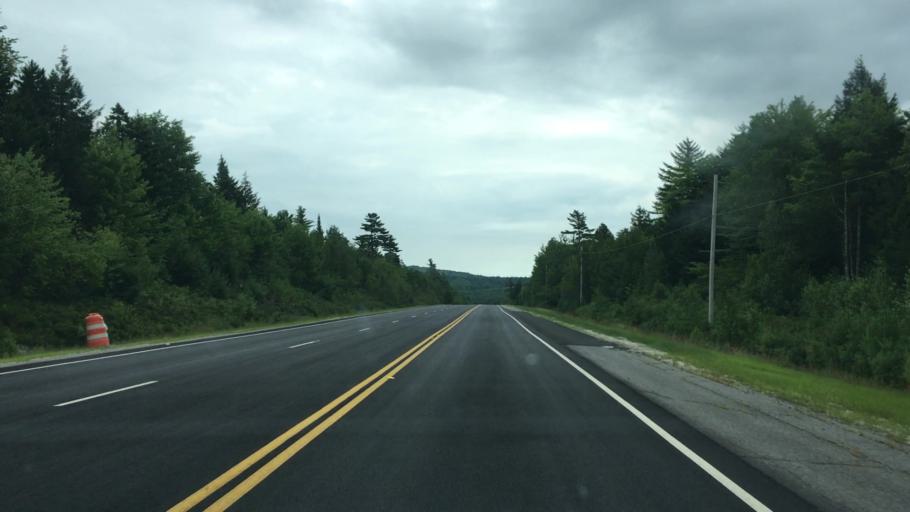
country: US
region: Maine
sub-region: Washington County
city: Cherryfield
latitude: 44.8765
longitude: -67.8865
